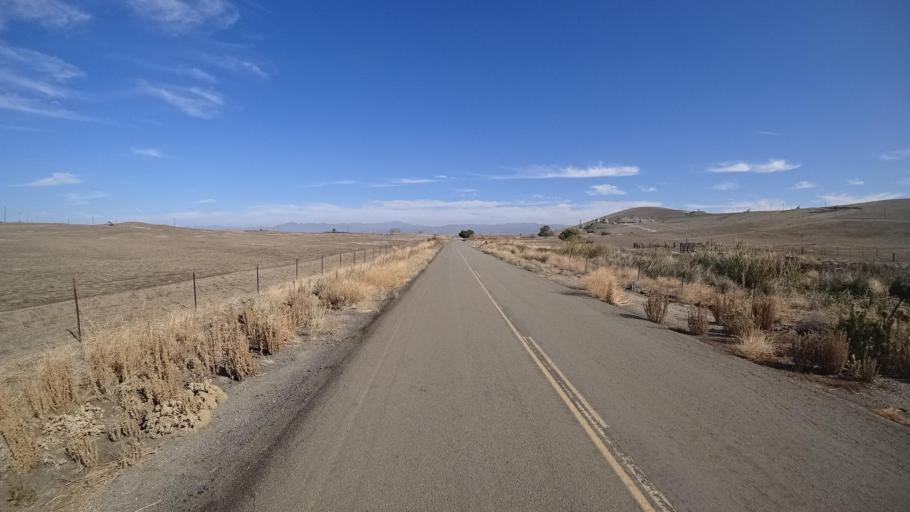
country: US
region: California
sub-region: Tulare County
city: Richgrove
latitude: 35.6318
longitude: -118.9639
